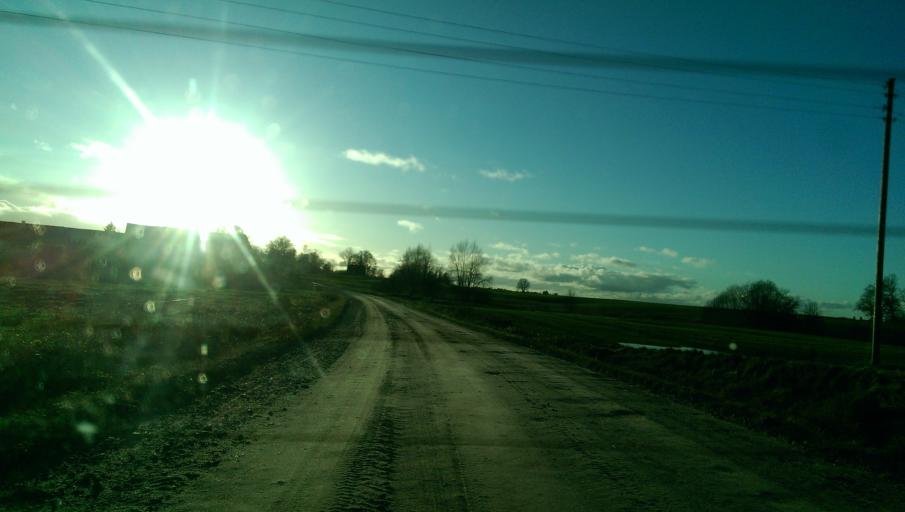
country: LV
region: Aizpute
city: Aizpute
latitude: 56.7465
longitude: 21.7499
